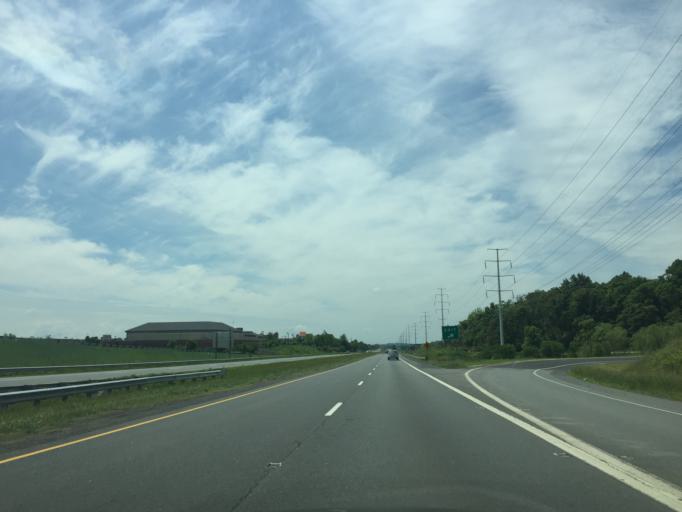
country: US
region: Virginia
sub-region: City of Winchester
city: Winchester
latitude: 39.2025
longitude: -78.1904
